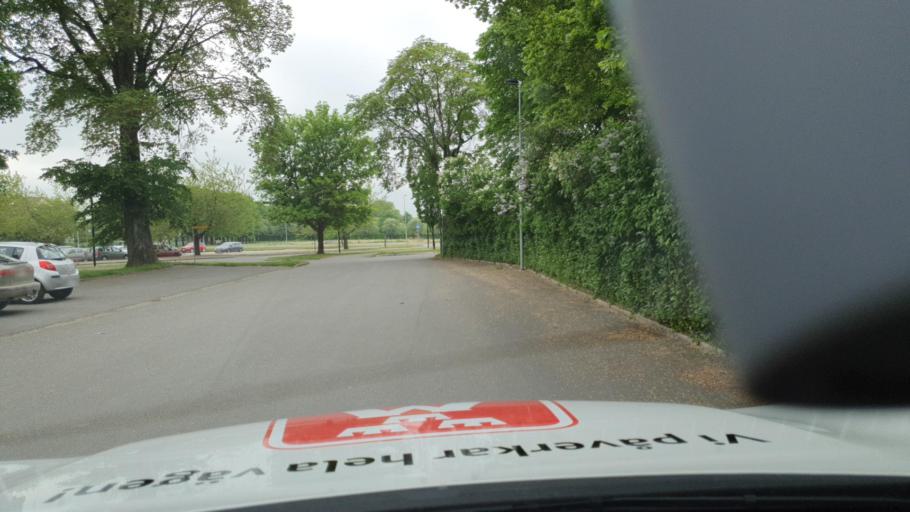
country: SE
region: Vaestra Goetaland
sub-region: Falkopings Kommun
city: Falkoeping
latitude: 58.1607
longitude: 13.5504
